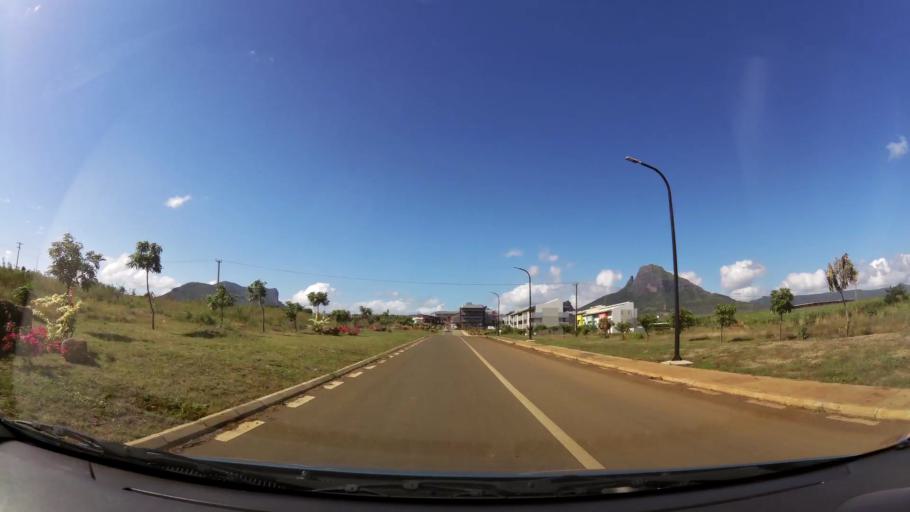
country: MU
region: Black River
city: Cascavelle
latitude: -20.2800
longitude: 57.3924
